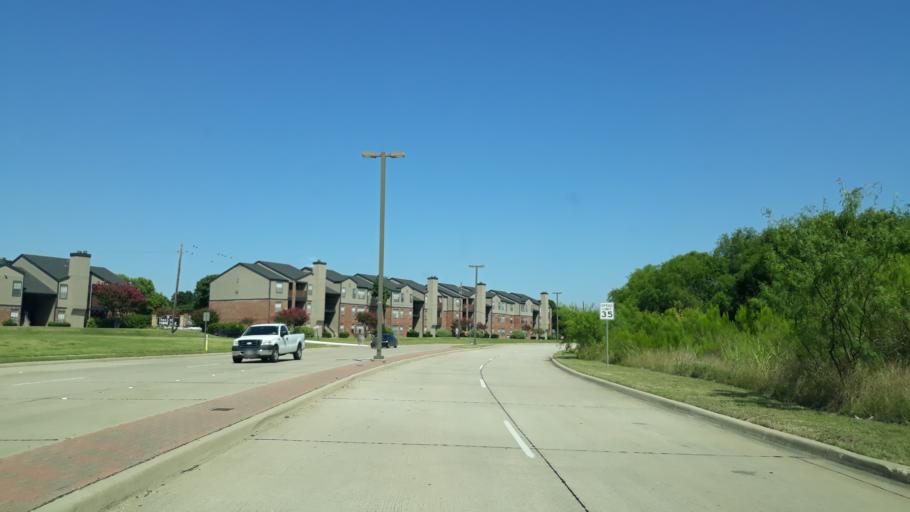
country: US
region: Texas
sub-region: Dallas County
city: Irving
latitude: 32.8245
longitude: -97.0130
